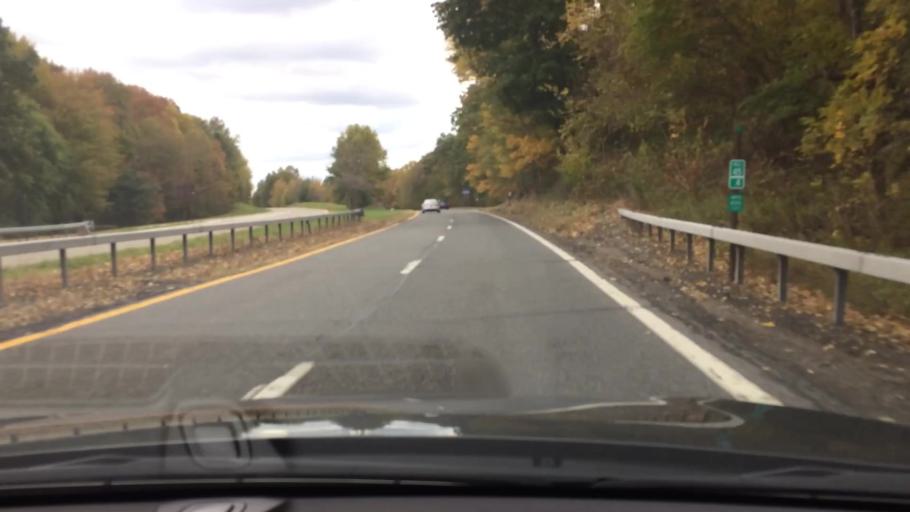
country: US
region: New York
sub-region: Dutchess County
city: Hillside Lake
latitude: 41.6430
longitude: -73.7877
